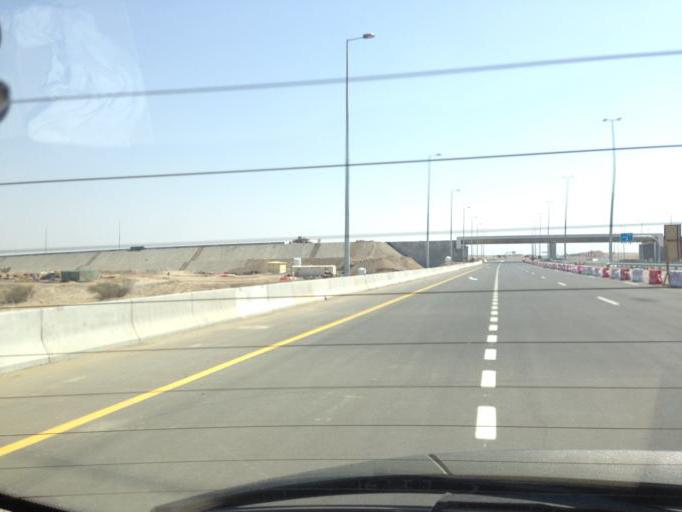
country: OM
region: Al Batinah
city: Rustaq
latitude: 23.5348
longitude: 57.5605
